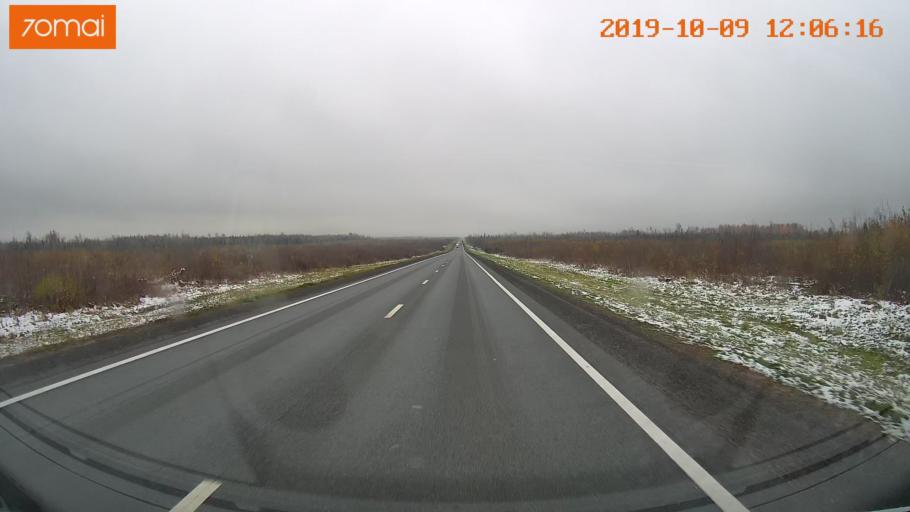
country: RU
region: Jaroslavl
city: Prechistoye
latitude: 58.6169
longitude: 40.3341
